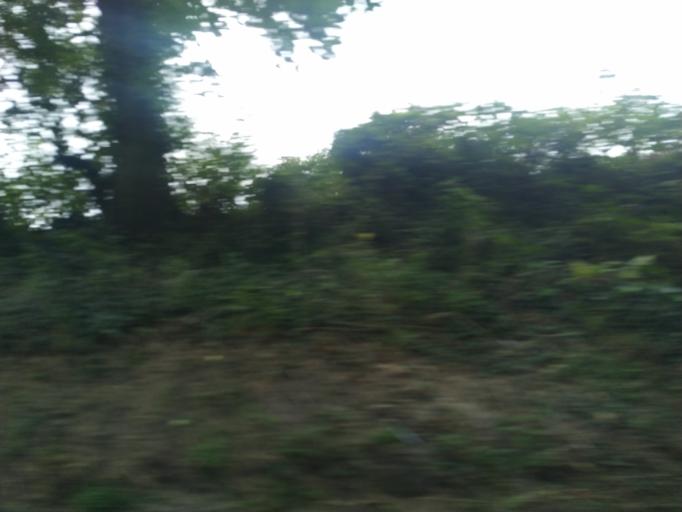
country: GB
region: England
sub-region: Dorset
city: Lytchett Matravers
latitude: 50.7617
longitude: -2.1284
